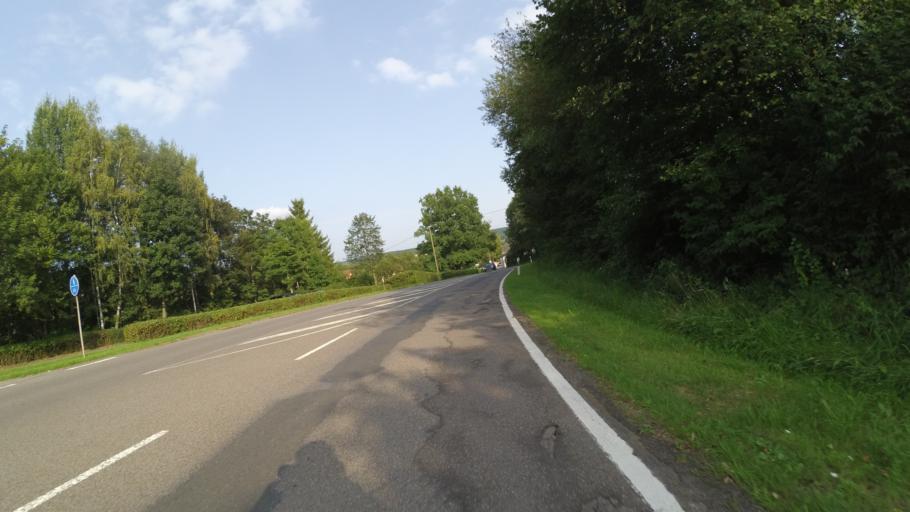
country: DE
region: Saarland
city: Wadern
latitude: 49.5433
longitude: 6.8871
